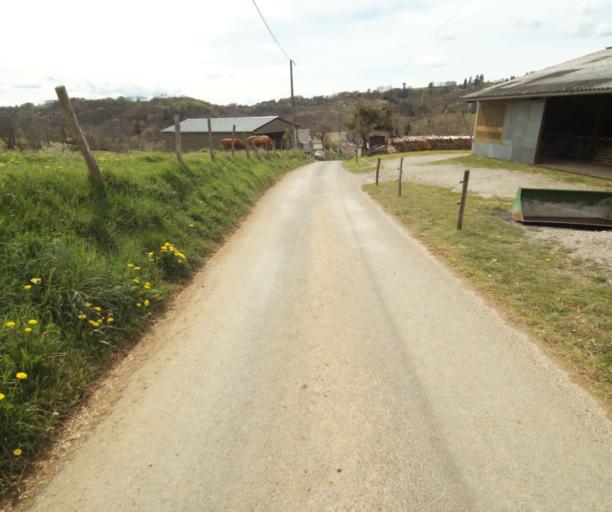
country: FR
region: Limousin
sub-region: Departement de la Correze
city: Laguenne
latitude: 45.2142
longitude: 1.8474
